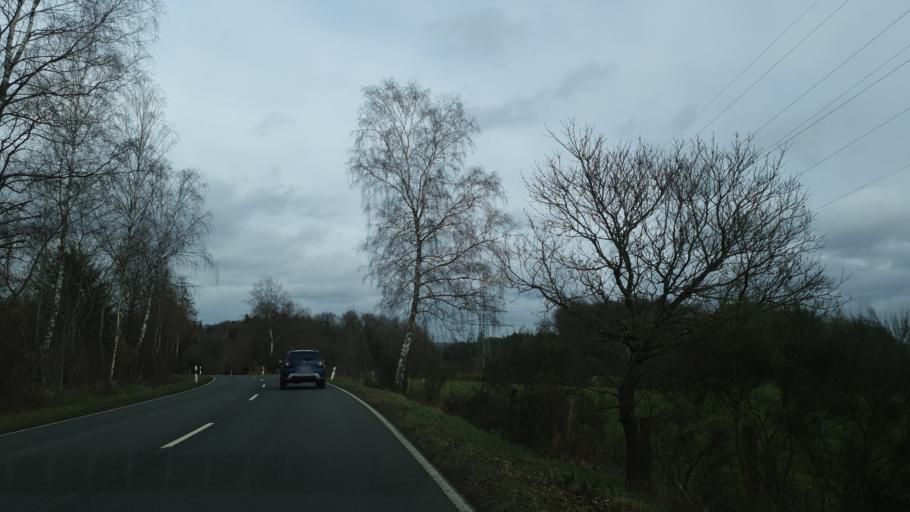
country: DE
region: Rheinland-Pfalz
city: Harschbach
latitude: 50.5804
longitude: 7.5953
